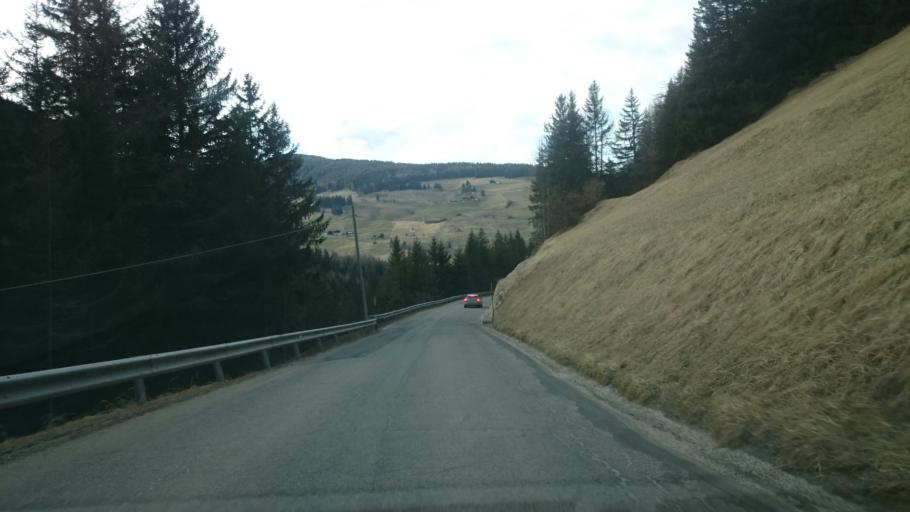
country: IT
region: Trentino-Alto Adige
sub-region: Bolzano
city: Braies
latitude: 46.7118
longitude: 12.1484
